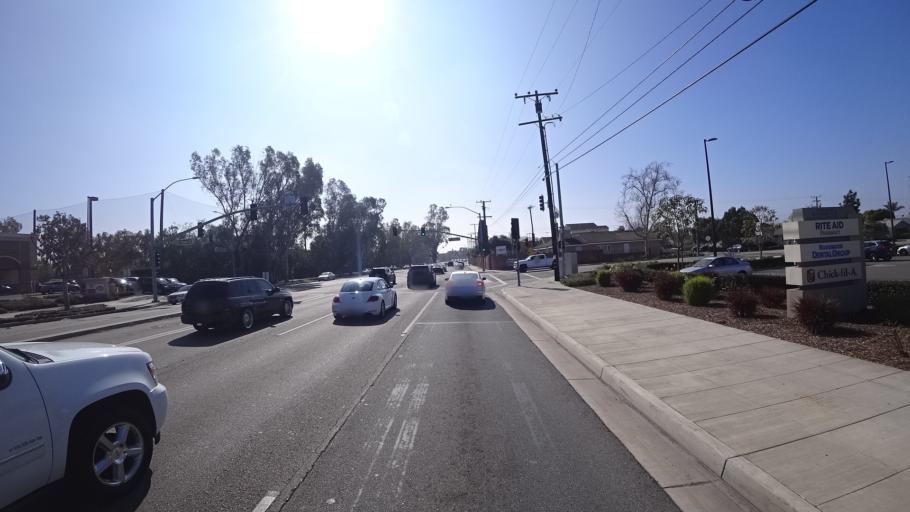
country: US
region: California
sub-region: Orange County
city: Rossmoor
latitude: 33.7807
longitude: -118.0721
